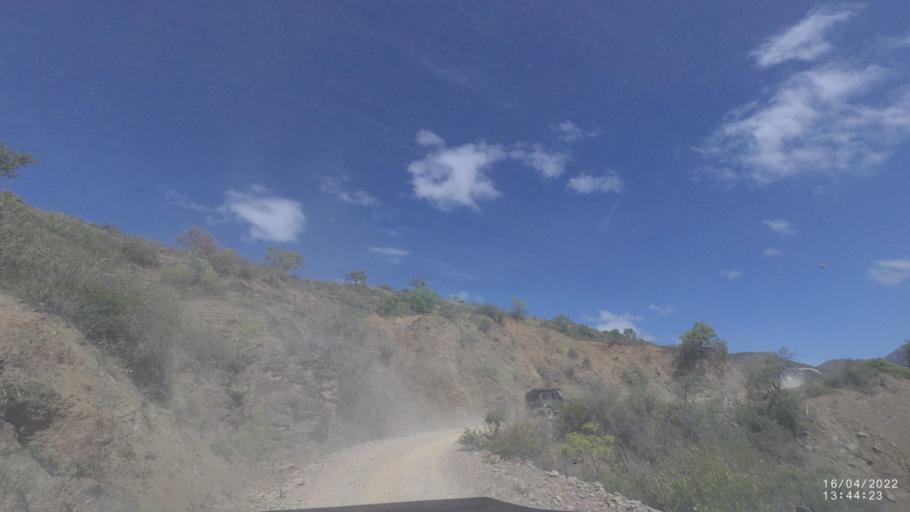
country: BO
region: Cochabamba
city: Mizque
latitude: -17.9983
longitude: -65.5917
